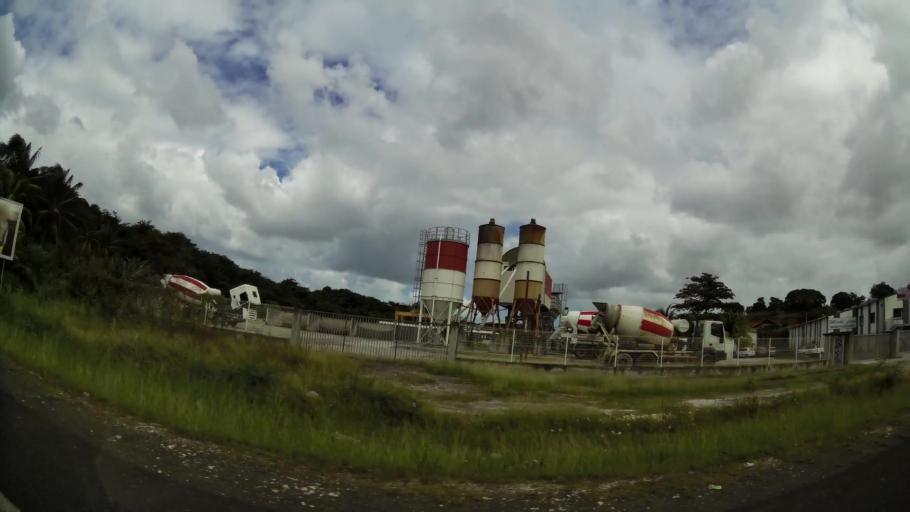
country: GP
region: Guadeloupe
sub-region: Guadeloupe
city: Baie-Mahault
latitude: 16.2558
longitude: -61.6009
